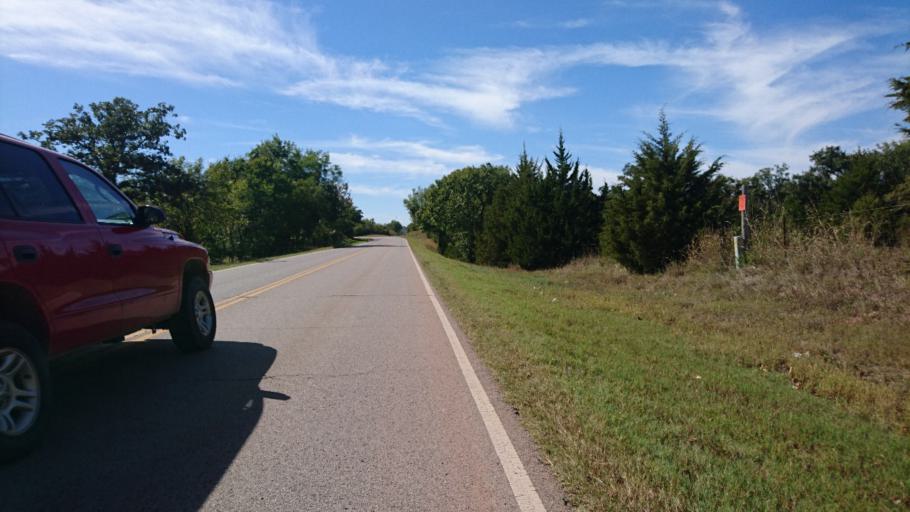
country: US
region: Oklahoma
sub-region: Lincoln County
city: Stroud
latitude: 35.7241
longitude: -96.7522
